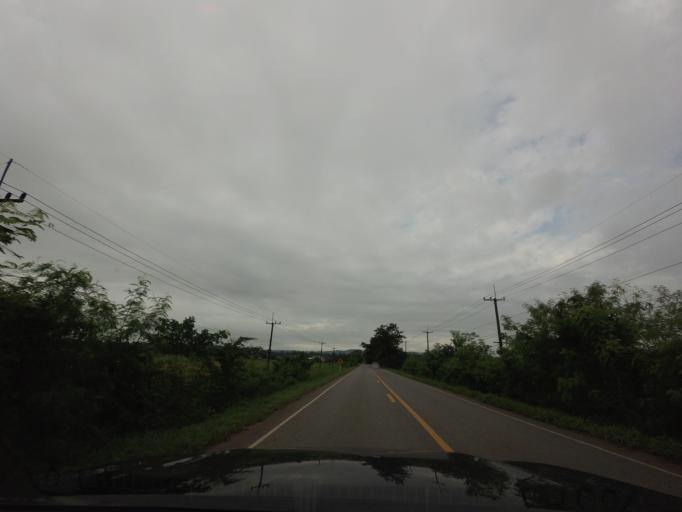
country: TH
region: Changwat Udon Thani
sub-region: Amphoe Ban Phue
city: Ban Phue
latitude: 17.7185
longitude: 102.3989
